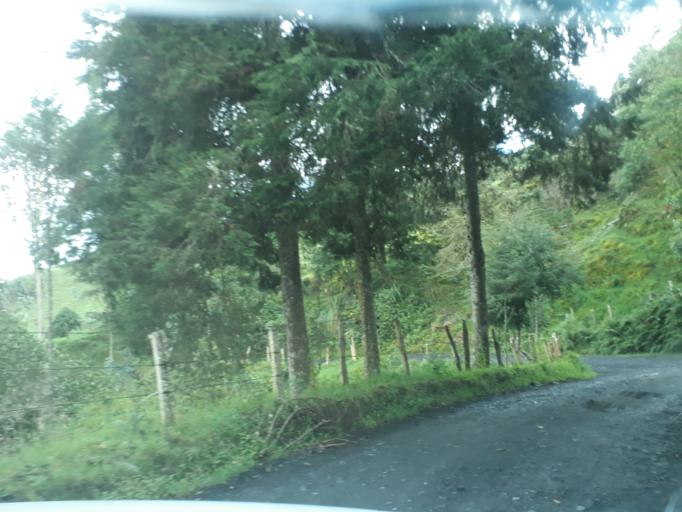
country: CO
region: Cundinamarca
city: La Mesa
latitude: 5.3309
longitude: -74.0550
